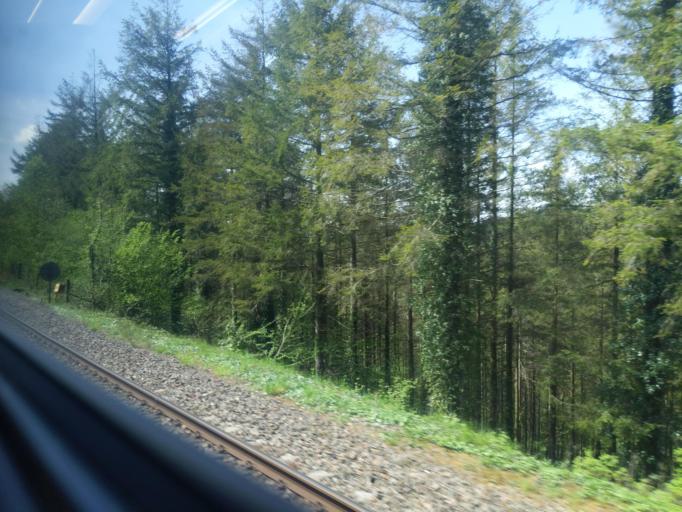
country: GB
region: England
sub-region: Cornwall
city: Liskeard
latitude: 50.4538
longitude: -4.5559
